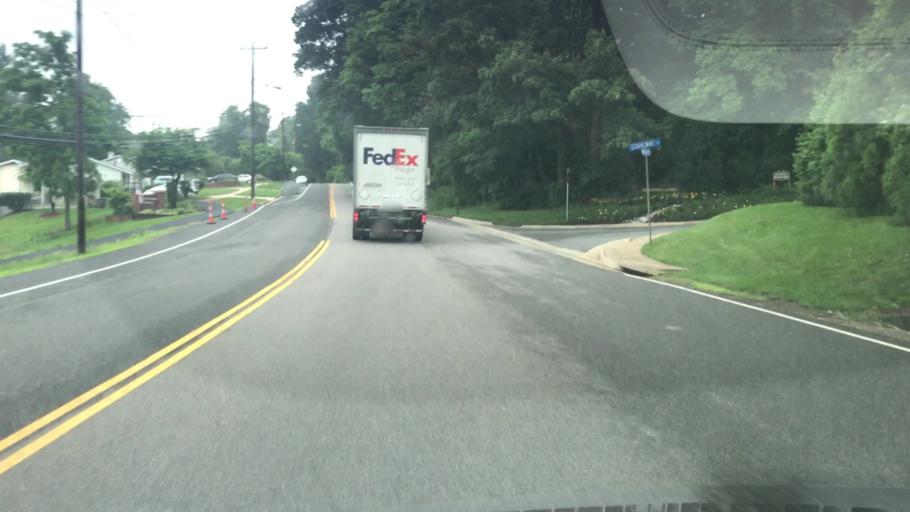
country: US
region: Virginia
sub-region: Fairfax County
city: Kings Park
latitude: 38.8127
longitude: -77.2348
